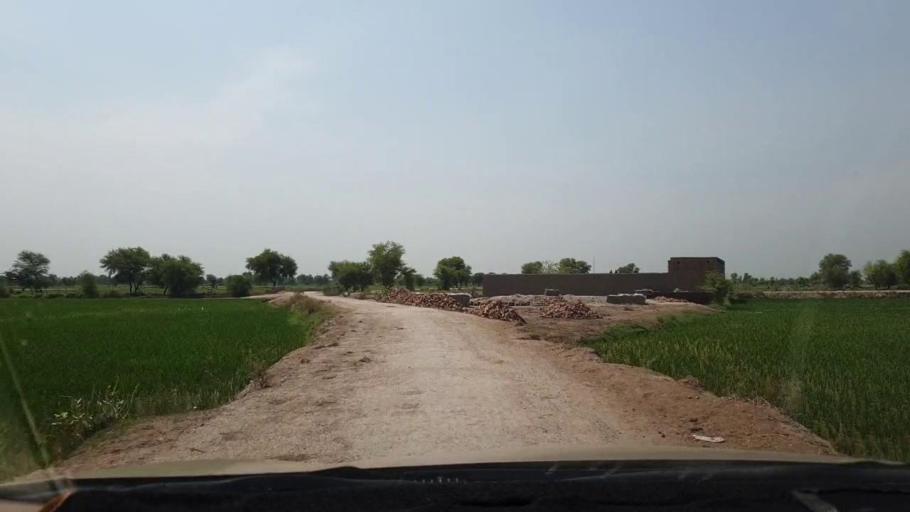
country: PK
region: Sindh
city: Naudero
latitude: 27.6457
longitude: 68.2746
